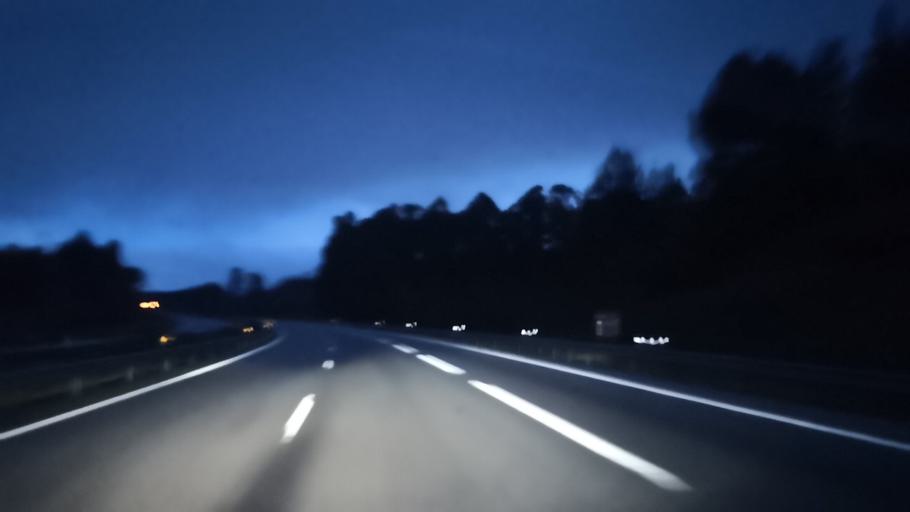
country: PT
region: Braga
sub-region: Guimaraes
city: Brito
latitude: 41.4720
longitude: -8.3776
